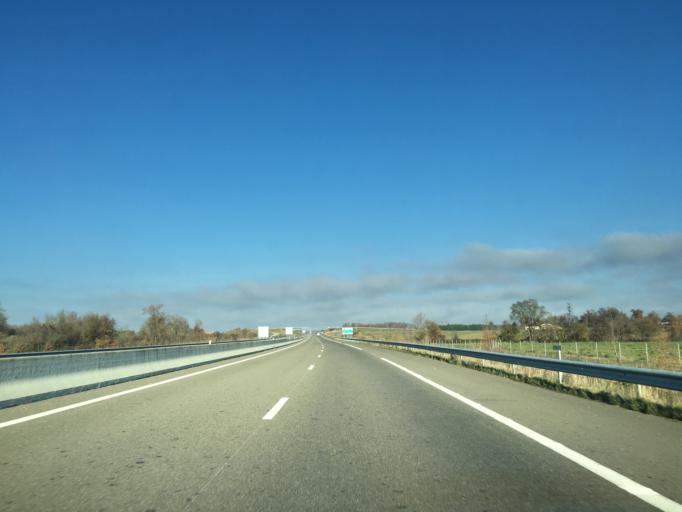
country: FR
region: Midi-Pyrenees
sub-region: Departement du Gers
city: Barcelonne-du-Gers
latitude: 43.7276
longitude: -0.2716
